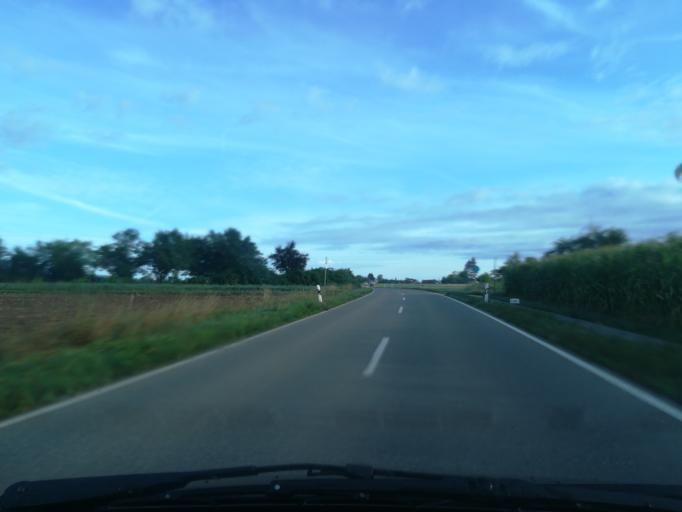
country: DE
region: Baden-Wuerttemberg
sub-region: Tuebingen Region
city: Sickenhausen
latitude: 48.5121
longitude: 9.1778
